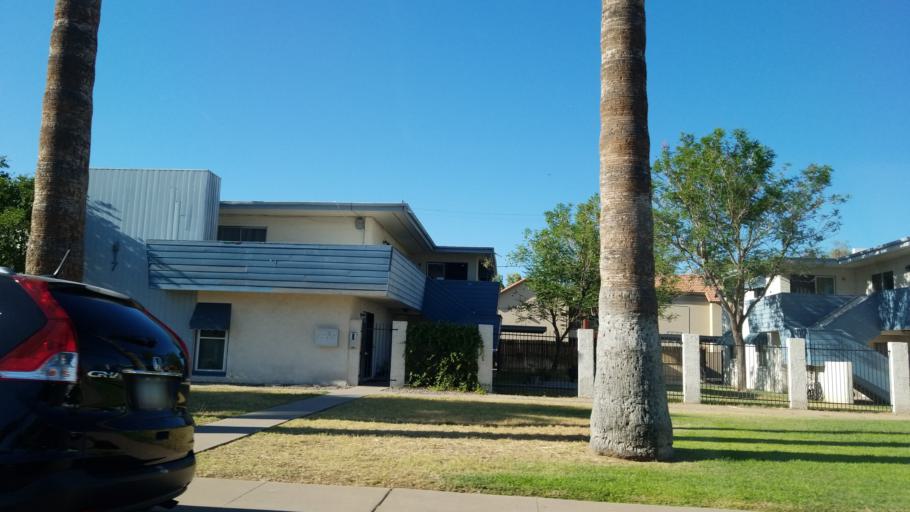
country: US
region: Arizona
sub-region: Maricopa County
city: Phoenix
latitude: 33.4790
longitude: -112.0664
